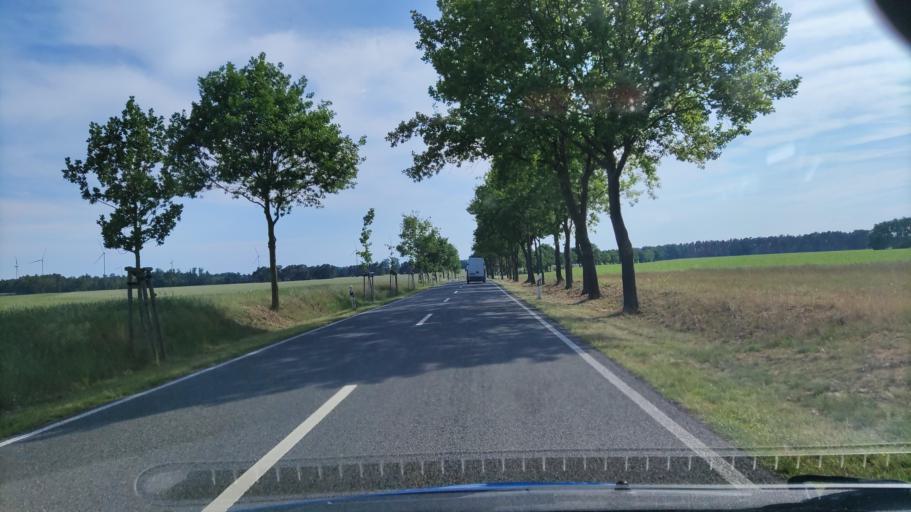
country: DE
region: Saxony-Anhalt
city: Klotze
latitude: 52.6855
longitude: 11.2405
